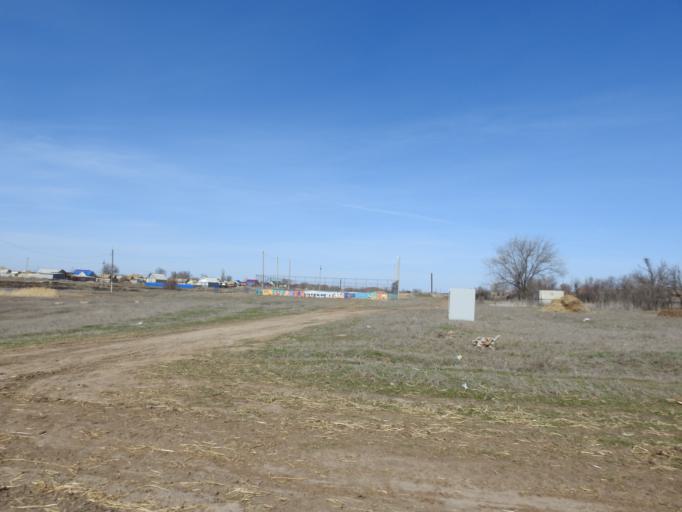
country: RU
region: Volgograd
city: Staraya Poltavka
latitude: 50.4302
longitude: 46.3949
